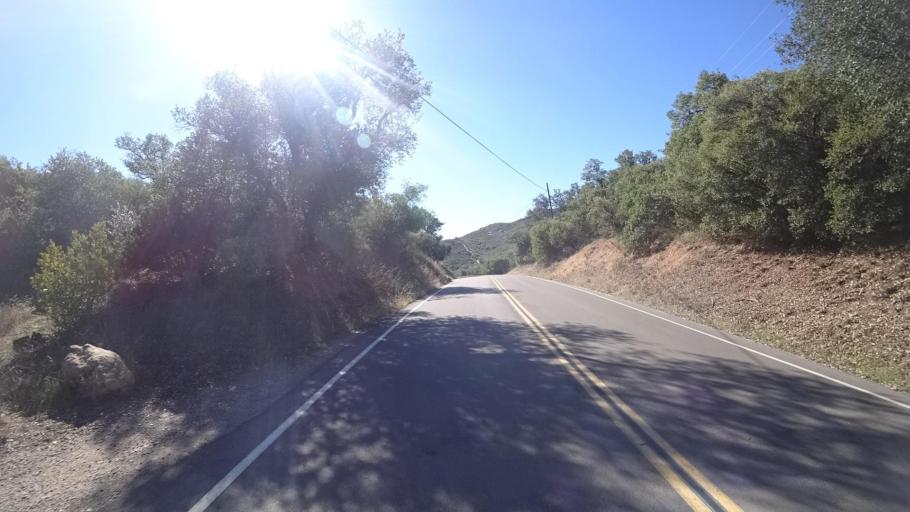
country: US
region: California
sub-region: San Diego County
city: Descanso
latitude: 32.8600
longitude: -116.6330
